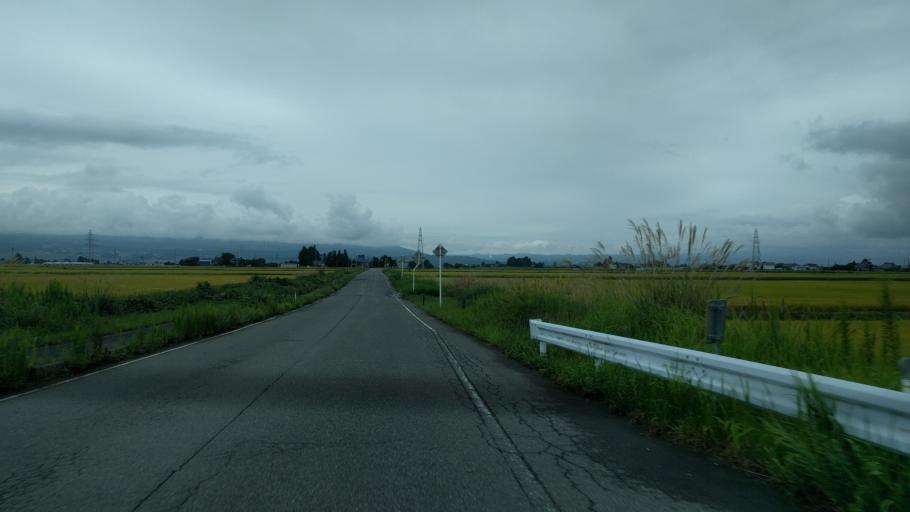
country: JP
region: Fukushima
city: Kitakata
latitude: 37.6173
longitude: 139.8429
